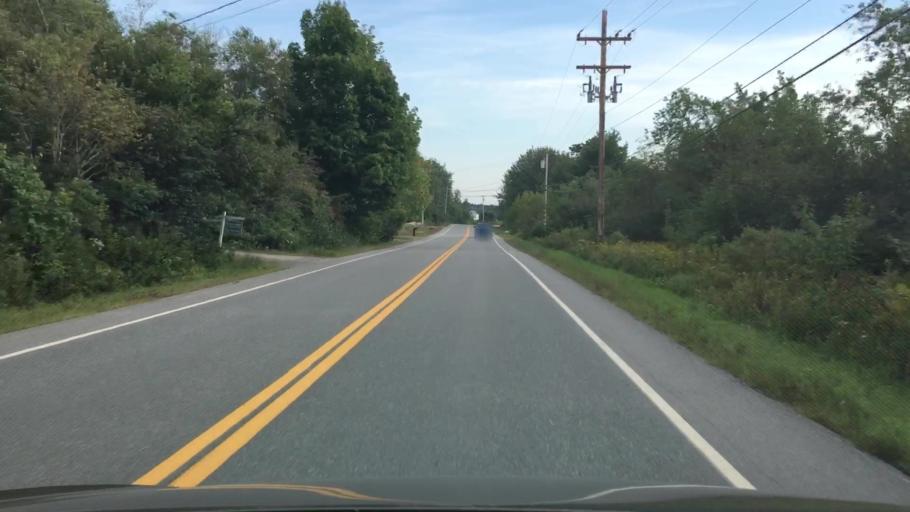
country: US
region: Maine
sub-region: Hancock County
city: Penobscot
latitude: 44.4695
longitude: -68.7818
